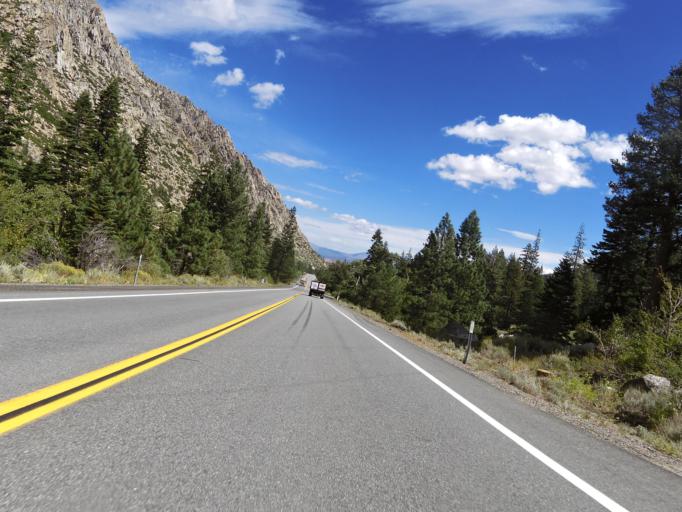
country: US
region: Nevada
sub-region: Douglas County
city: Gardnerville Ranchos
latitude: 38.7646
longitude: -119.8499
